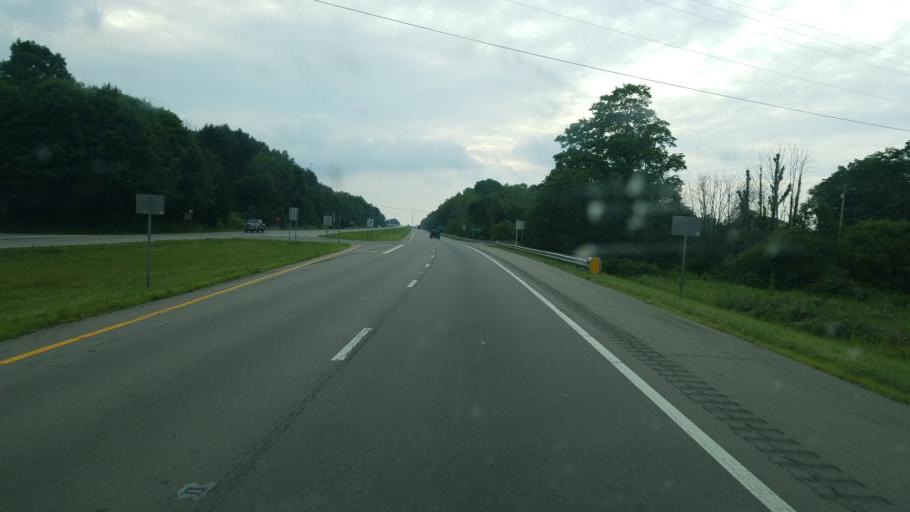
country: US
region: Ohio
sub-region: Wayne County
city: Wooster
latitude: 40.7996
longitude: -82.0089
